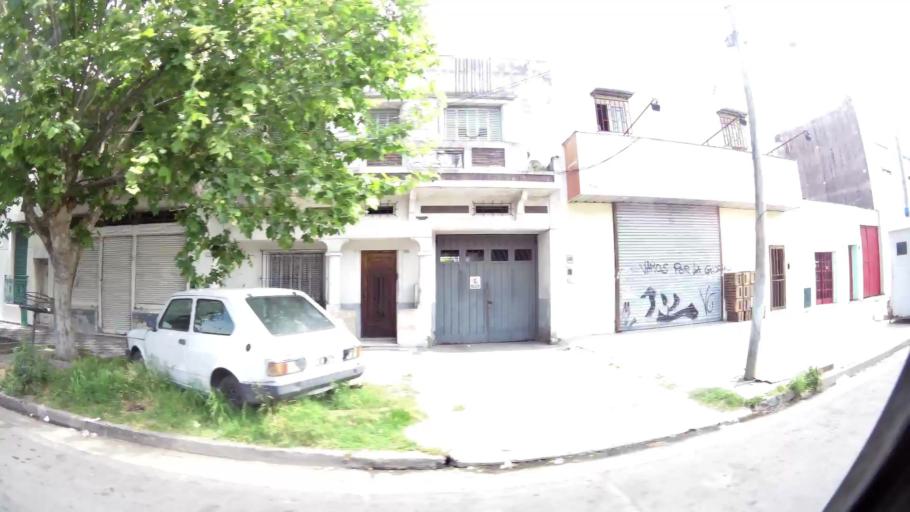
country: AR
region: Buenos Aires
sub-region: Partido de Avellaneda
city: Avellaneda
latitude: -34.6677
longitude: -58.4012
